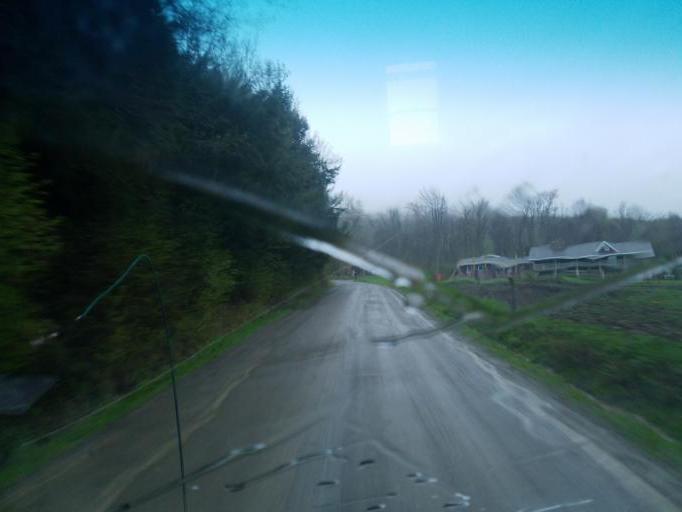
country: US
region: Pennsylvania
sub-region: Tioga County
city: Westfield
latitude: 41.9415
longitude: -77.6958
